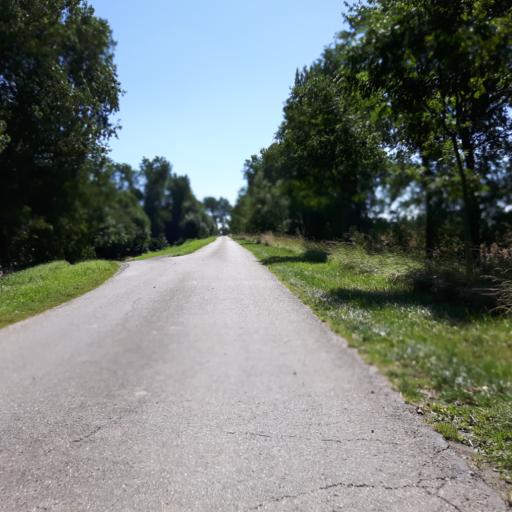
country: NL
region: Zeeland
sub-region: Gemeente Goes
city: Goes
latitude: 51.5659
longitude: 3.8125
